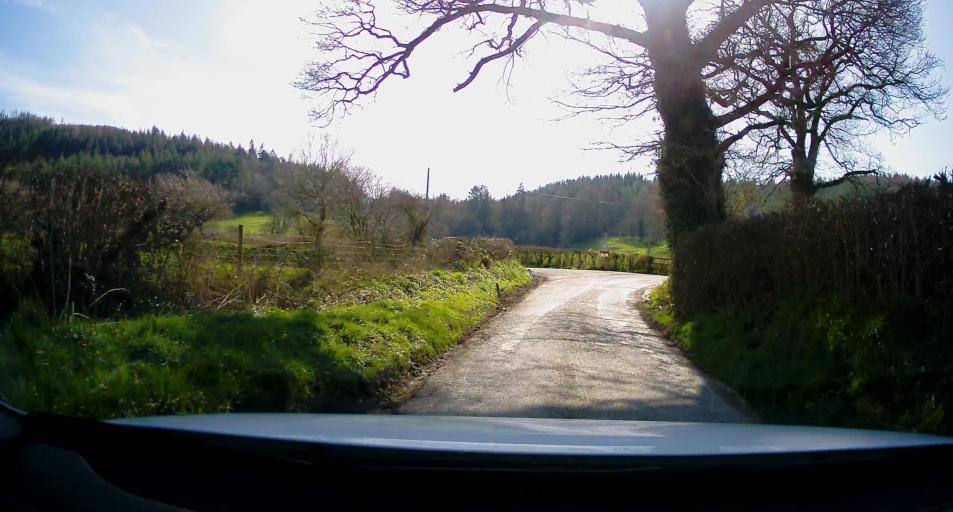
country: GB
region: Wales
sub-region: County of Ceredigion
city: Lledrod
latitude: 52.3277
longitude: -3.9552
